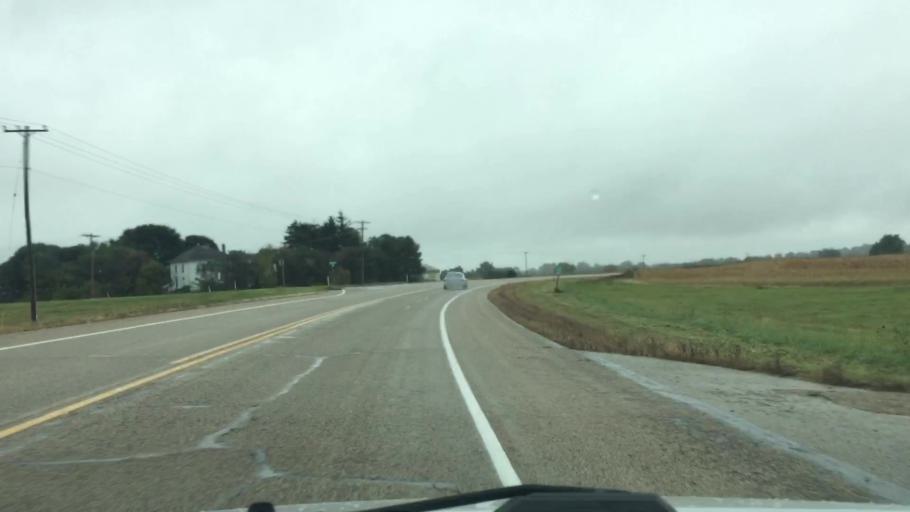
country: US
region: Wisconsin
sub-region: Jefferson County
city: Palmyra
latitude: 42.8626
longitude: -88.6501
